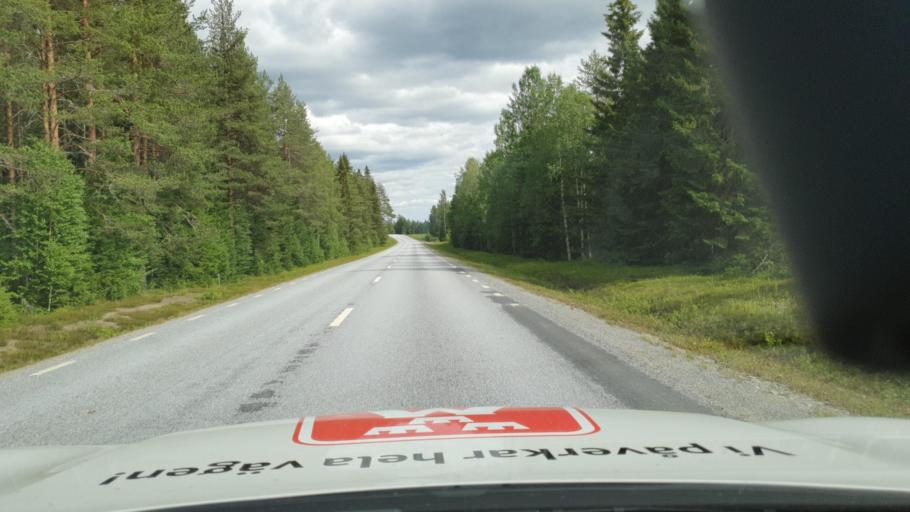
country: SE
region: Vaesterbotten
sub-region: Bjurholms Kommun
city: Bjurholm
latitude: 63.9279
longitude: 19.0167
